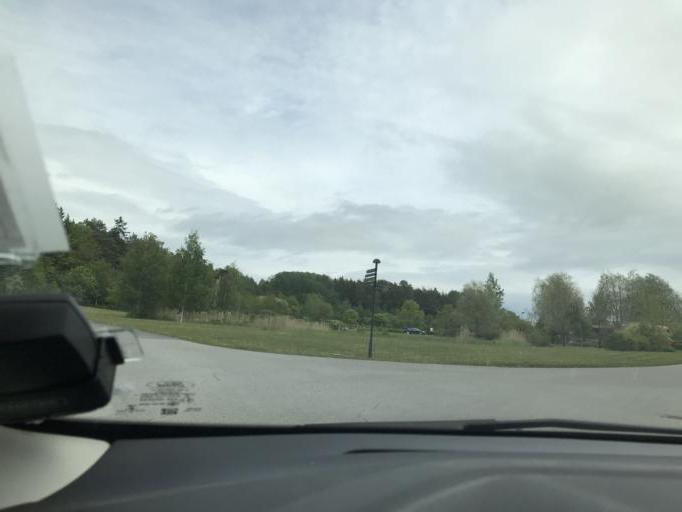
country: SE
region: Stockholm
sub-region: Botkyrka Kommun
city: Alby
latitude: 59.2184
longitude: 17.8496
